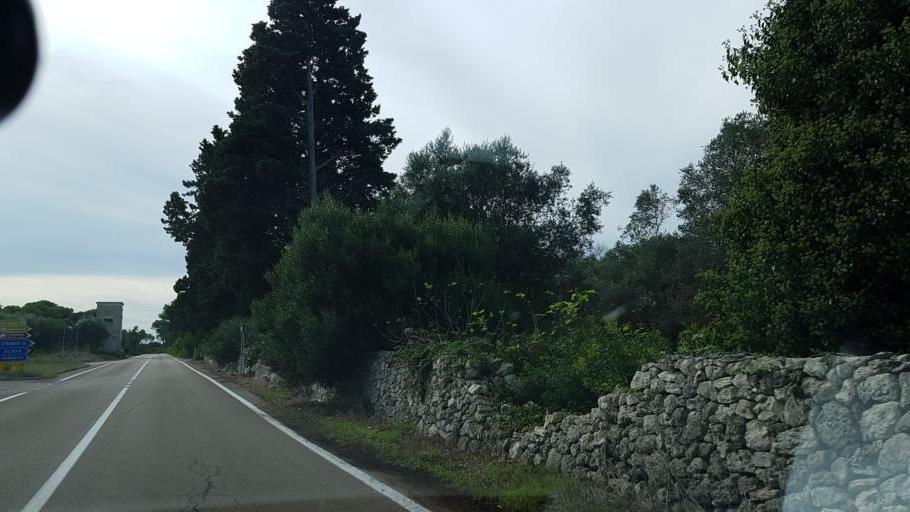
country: IT
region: Apulia
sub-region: Provincia di Lecce
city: Struda
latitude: 40.3864
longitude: 18.2971
